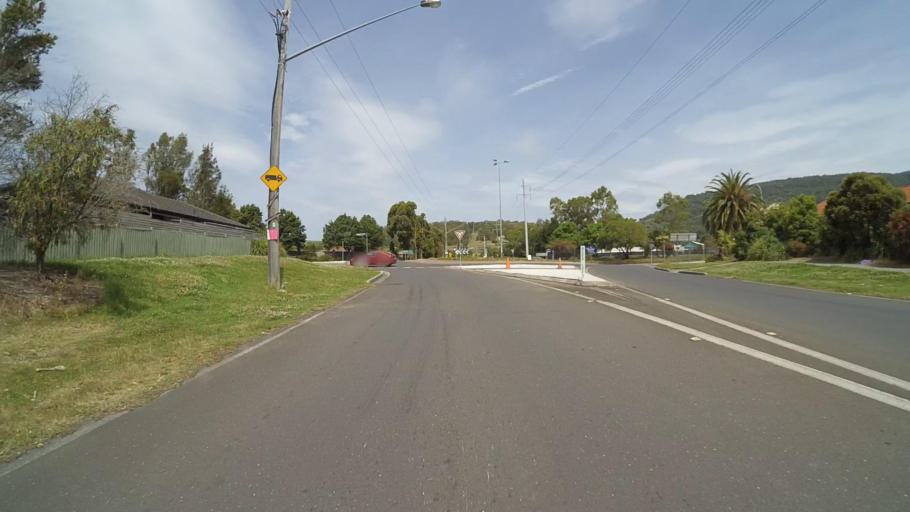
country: AU
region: New South Wales
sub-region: Shellharbour
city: Albion Park Rail
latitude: -34.5903
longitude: 150.7808
